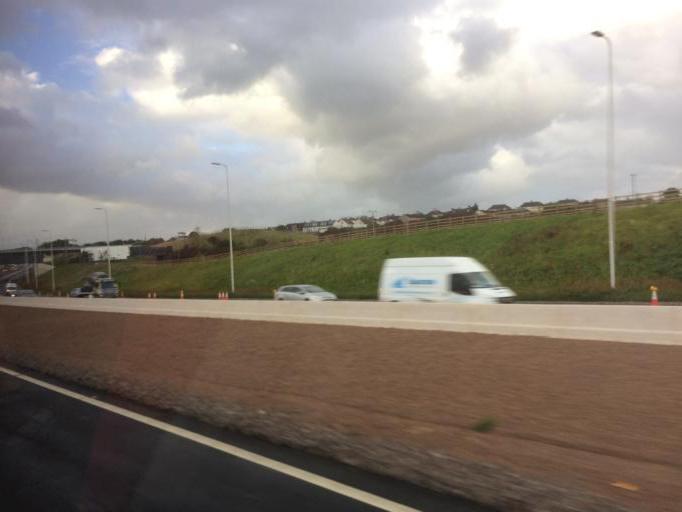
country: GB
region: Scotland
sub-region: South Lanarkshire
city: Uddingston
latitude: 55.8475
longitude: -4.0767
